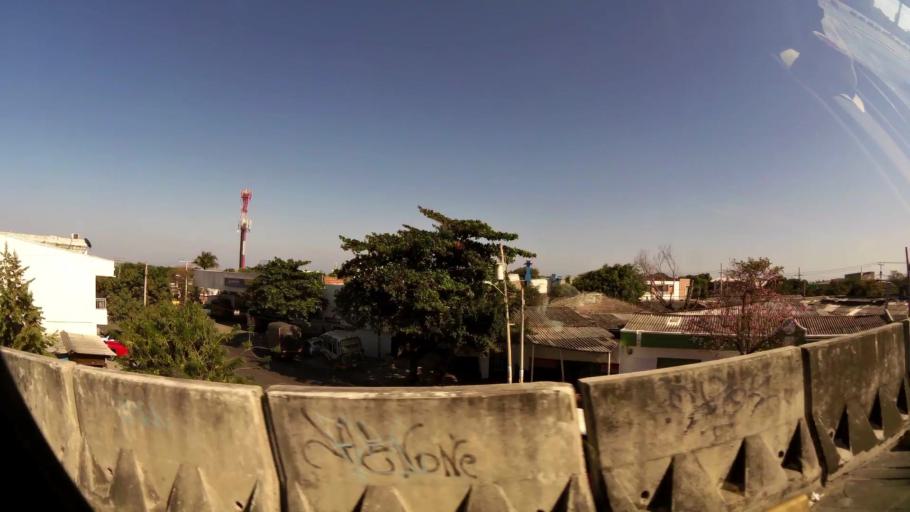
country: CO
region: Atlantico
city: Barranquilla
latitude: 10.9647
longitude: -74.7918
